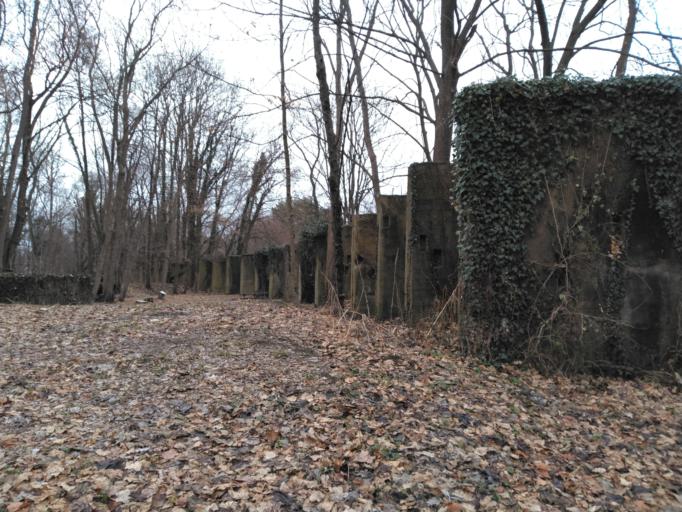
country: US
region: Pennsylvania
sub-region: Lancaster County
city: Marietta
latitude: 40.0584
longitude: -76.5350
